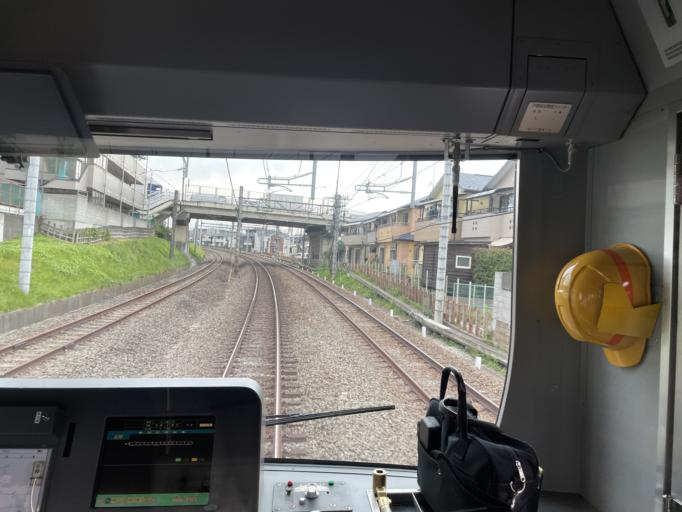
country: JP
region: Saitama
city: Tokorozawa
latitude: 35.7888
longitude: 139.4820
